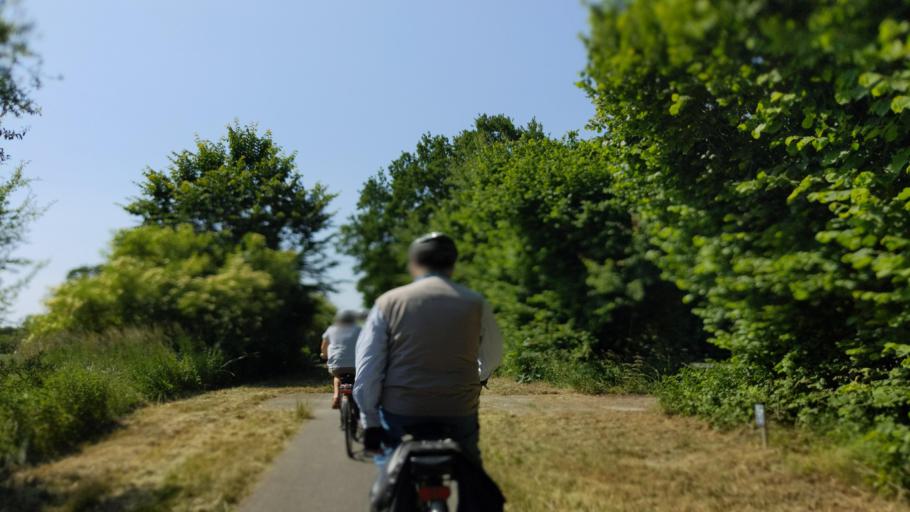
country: DE
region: Schleswig-Holstein
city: Berkenthin
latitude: 53.7469
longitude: 10.6559
